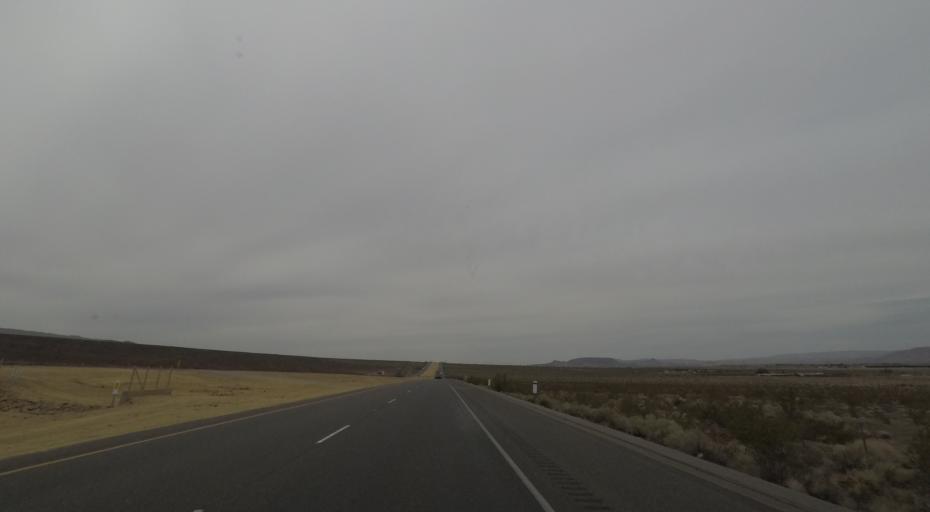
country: US
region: California
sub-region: San Bernardino County
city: Barstow
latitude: 34.8373
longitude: -116.7715
